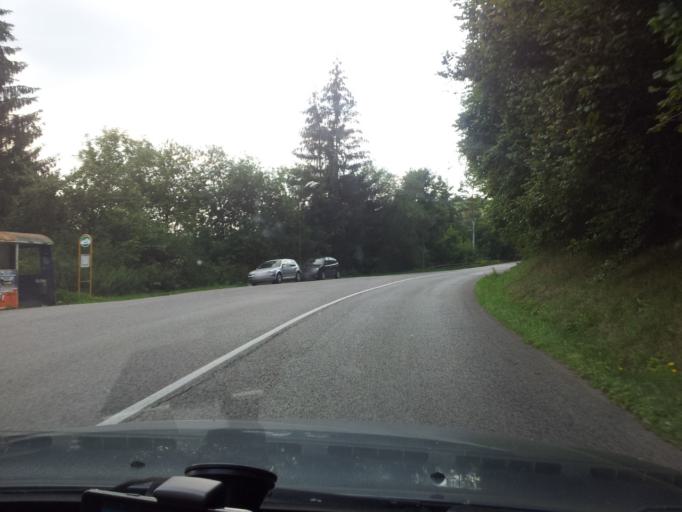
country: SK
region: Zilinsky
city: Tvrdosin
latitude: 49.3756
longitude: 19.5548
